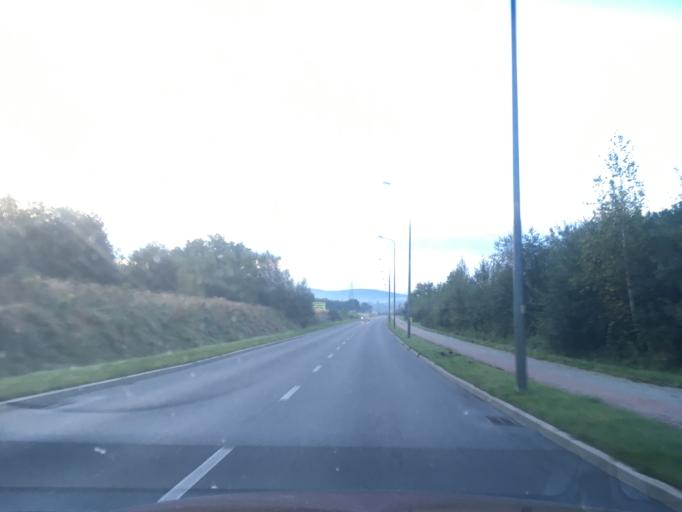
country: PL
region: Lower Silesian Voivodeship
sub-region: Powiat zgorzelecki
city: Bogatynia
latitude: 50.9211
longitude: 14.9493
